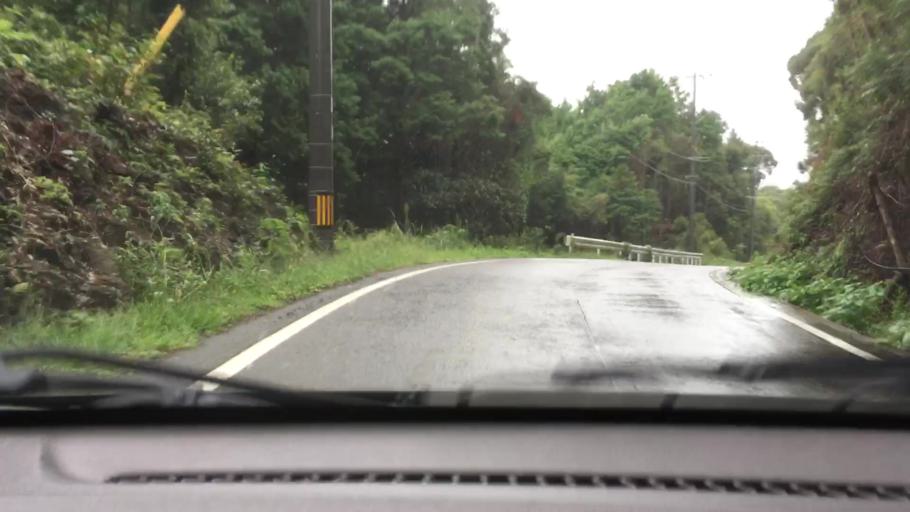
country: JP
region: Nagasaki
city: Togitsu
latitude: 32.8723
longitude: 129.7646
